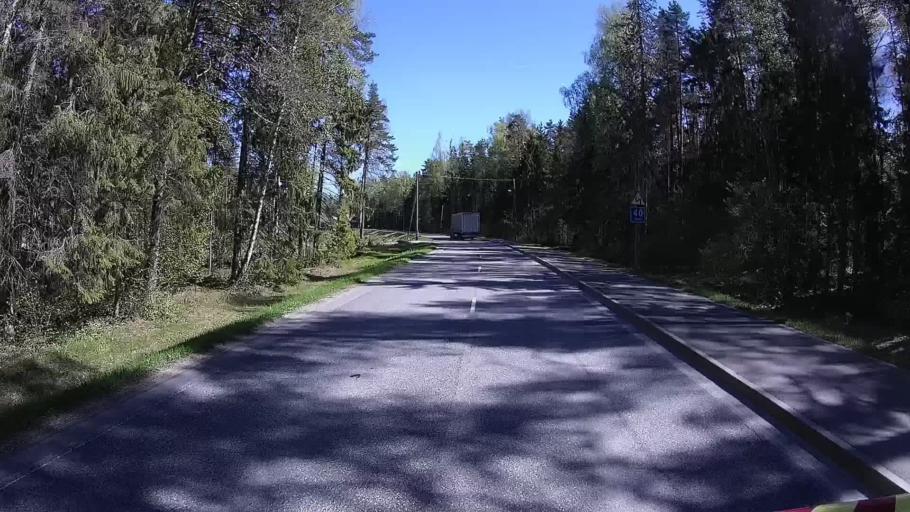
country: EE
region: Harju
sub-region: Kuusalu vald
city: Kuusalu
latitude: 59.2719
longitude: 25.6347
